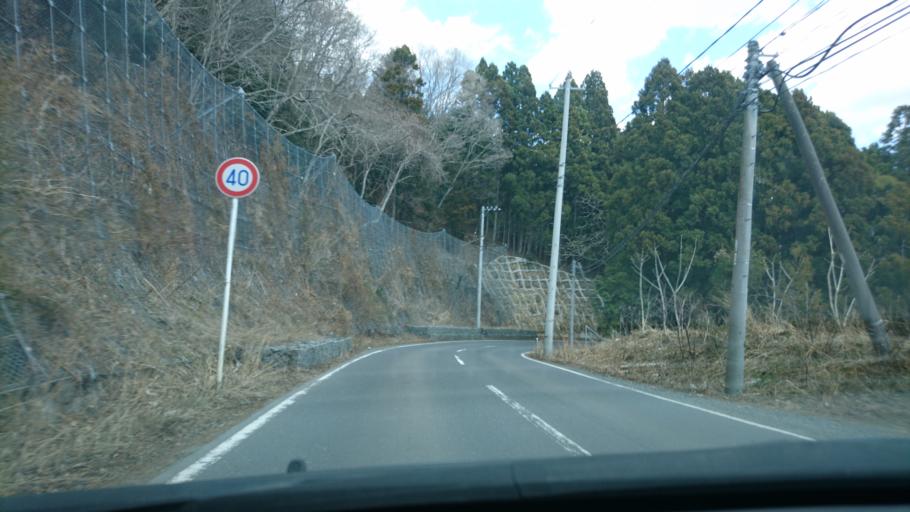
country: JP
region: Miyagi
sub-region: Oshika Gun
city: Onagawa Cho
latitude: 38.4453
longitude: 141.4861
